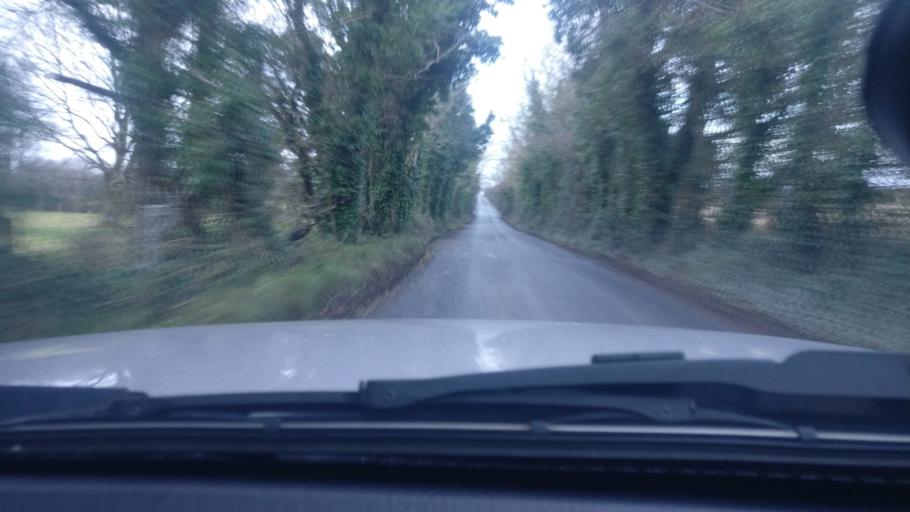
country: IE
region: Connaught
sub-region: County Galway
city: Loughrea
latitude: 53.1941
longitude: -8.5087
